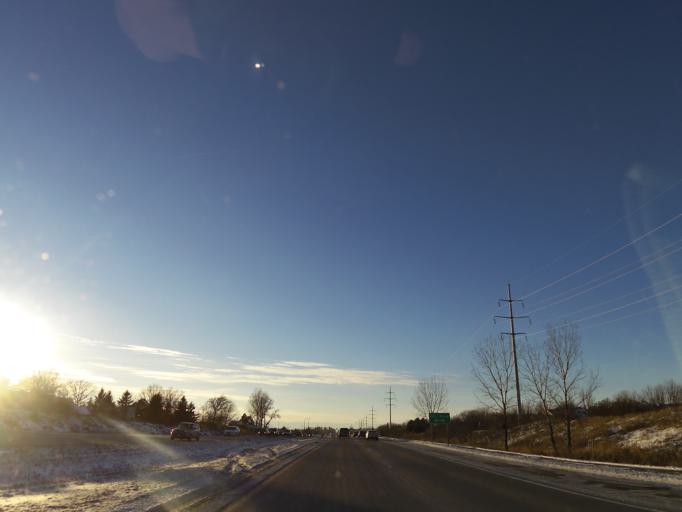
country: US
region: Minnesota
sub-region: Carver County
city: Chanhassen
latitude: 44.8619
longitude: -93.5069
